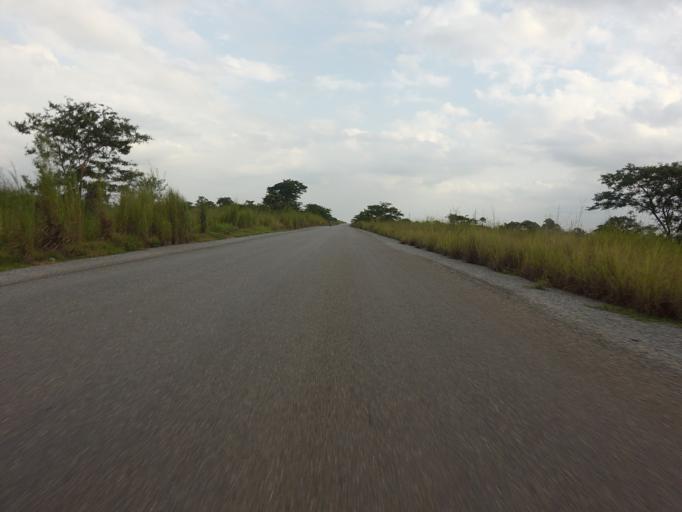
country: GH
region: Volta
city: Ho
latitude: 6.4172
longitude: 0.5205
